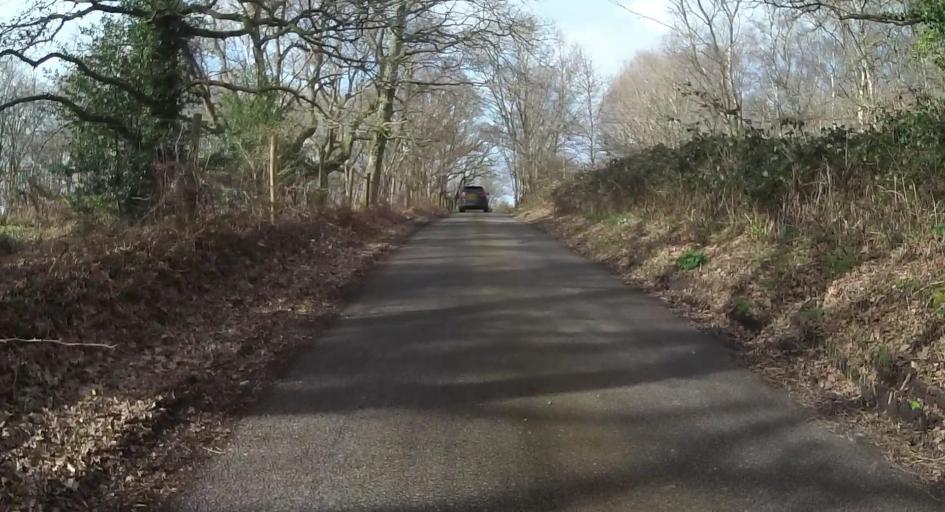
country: GB
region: England
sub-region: West Berkshire
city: Thatcham
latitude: 51.3741
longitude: -1.2550
